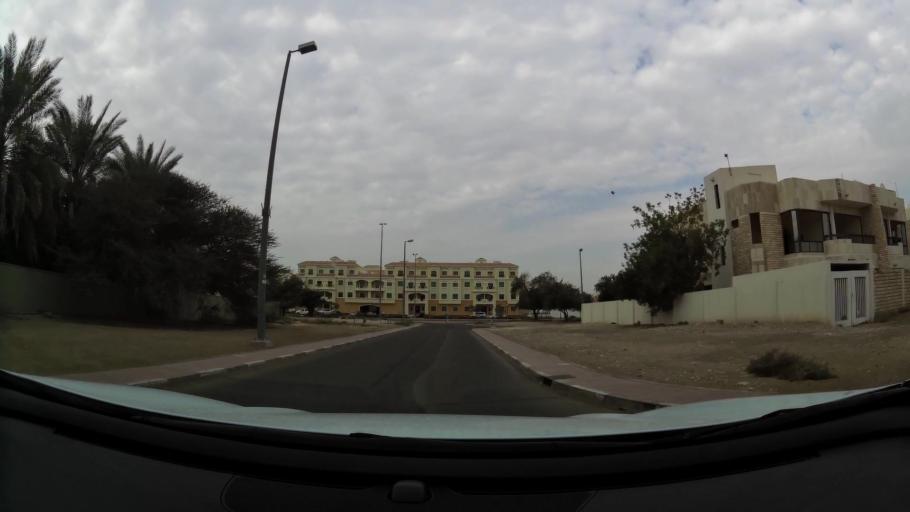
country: AE
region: Abu Dhabi
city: Al Ain
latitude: 24.2268
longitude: 55.7318
